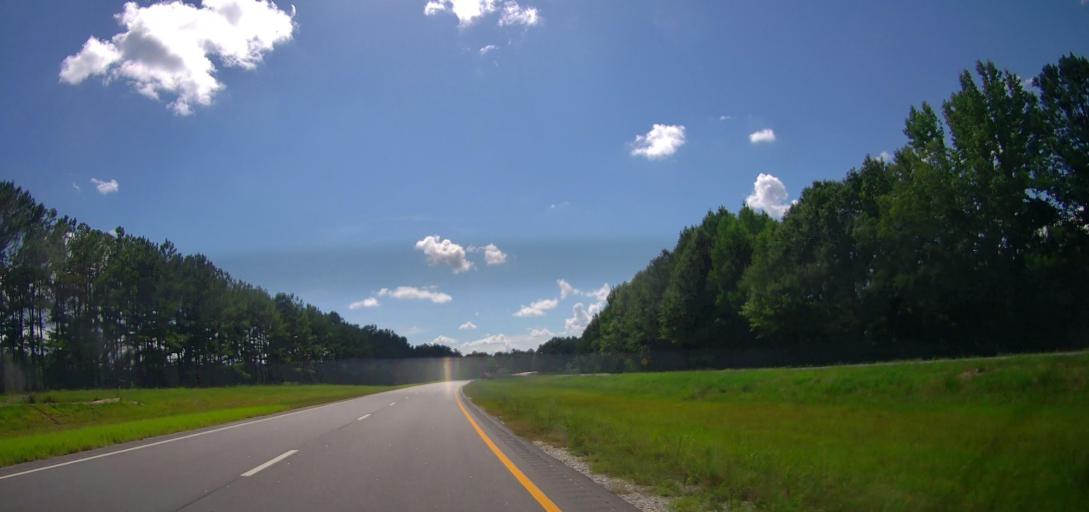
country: US
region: Alabama
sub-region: Macon County
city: Tuskegee
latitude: 32.3783
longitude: -85.7799
